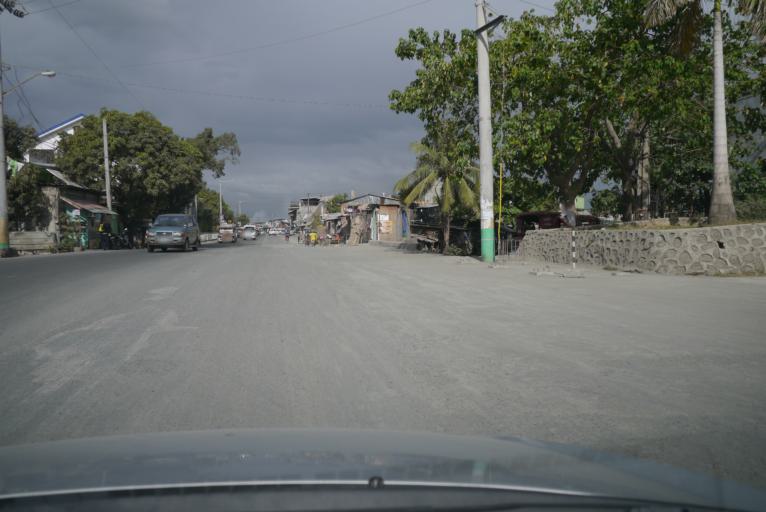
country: PH
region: Calabarzon
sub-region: Province of Rizal
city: Taytay
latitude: 14.5437
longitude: 121.1264
